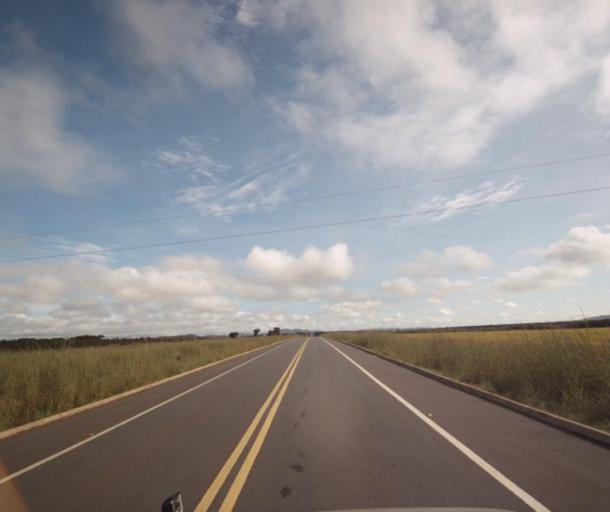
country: BR
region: Goias
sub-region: Barro Alto
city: Barro Alto
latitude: -15.2292
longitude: -48.6943
